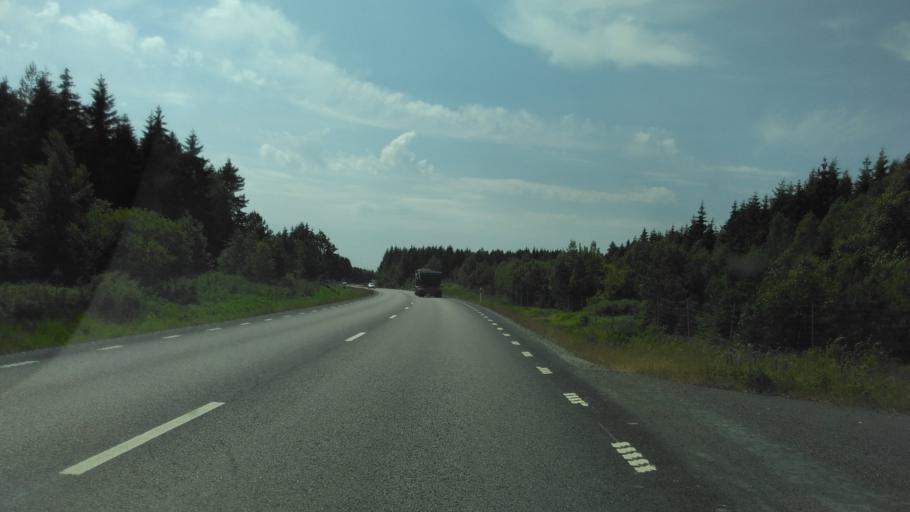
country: SE
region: Vaestra Goetaland
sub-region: Lidkopings Kommun
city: Lidkoping
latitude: 58.4504
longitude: 12.9812
